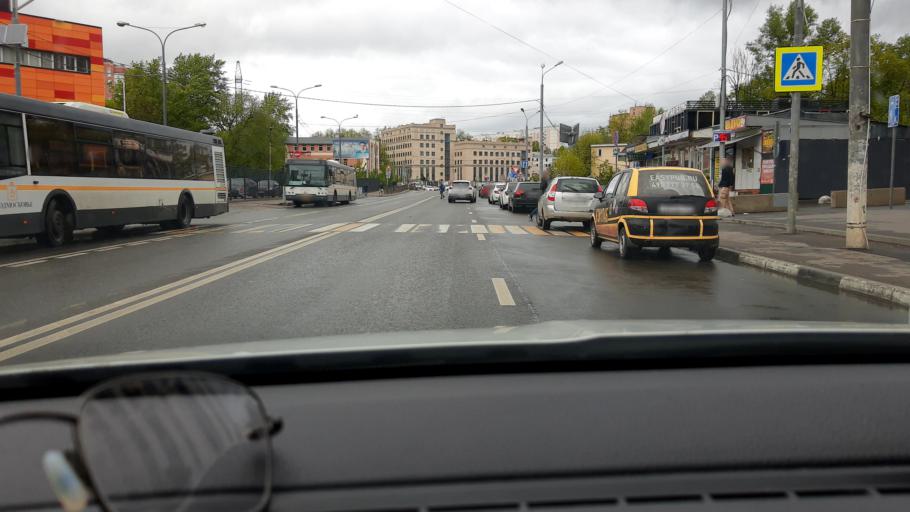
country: RU
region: Moskovskaya
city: Pavshino
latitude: 55.8165
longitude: 37.3410
